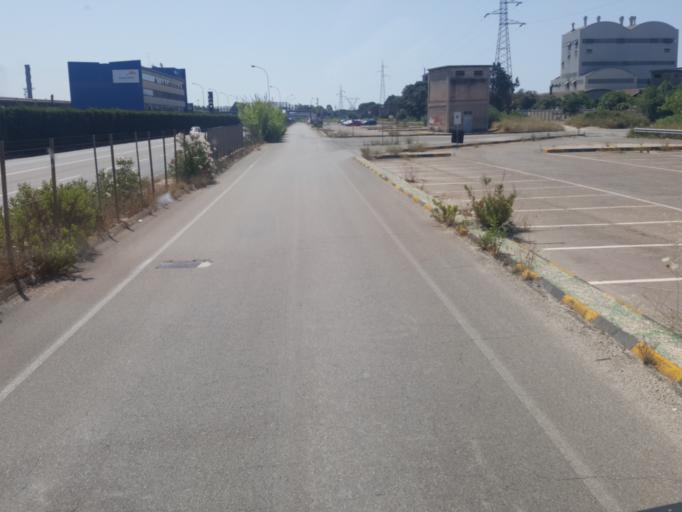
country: IT
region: Apulia
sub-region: Provincia di Taranto
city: Statte
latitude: 40.5025
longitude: 17.1990
